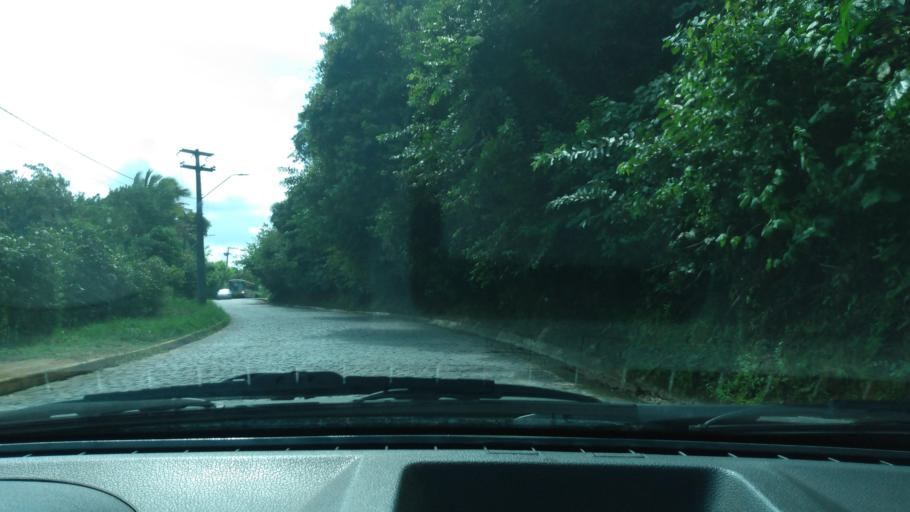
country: BR
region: Pernambuco
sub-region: Cabo De Santo Agostinho
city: Cabo
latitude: -8.3530
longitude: -34.9516
